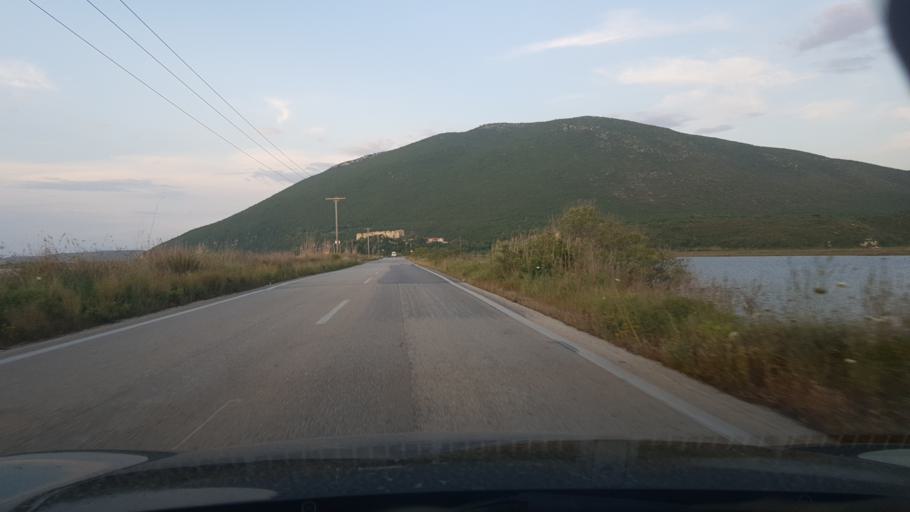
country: GR
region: Ionian Islands
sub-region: Lefkada
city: Lefkada
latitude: 38.8453
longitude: 20.7305
